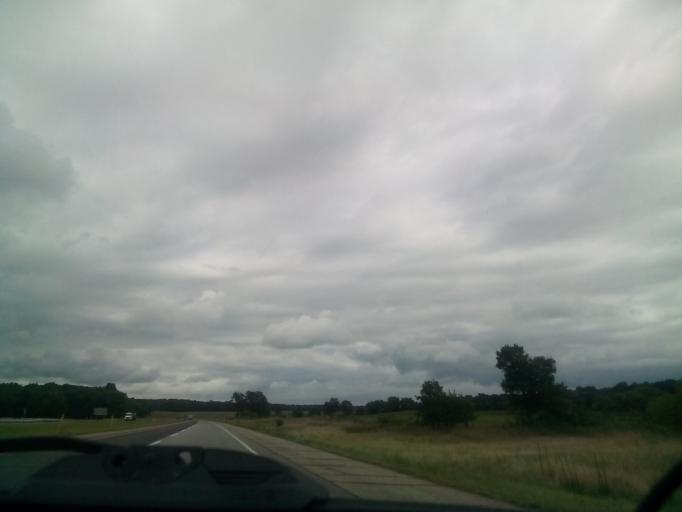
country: US
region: Michigan
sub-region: Saint Joseph County
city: Sturgis
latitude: 41.7397
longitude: -85.2891
